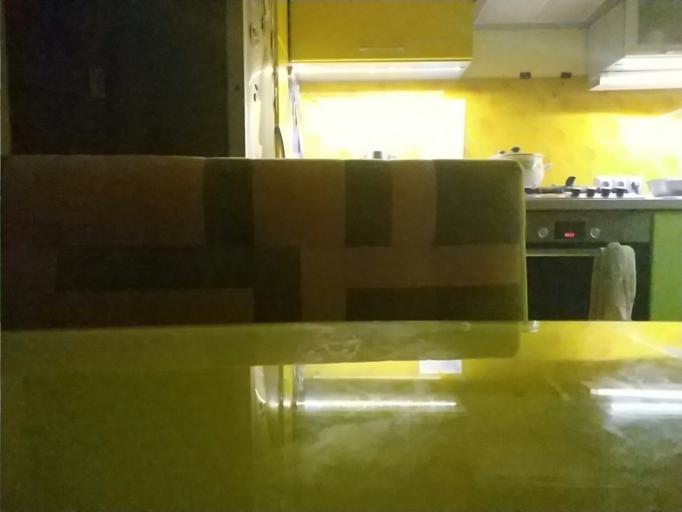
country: RU
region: Republic of Karelia
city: Pyaozerskiy
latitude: 65.4105
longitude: 30.6510
